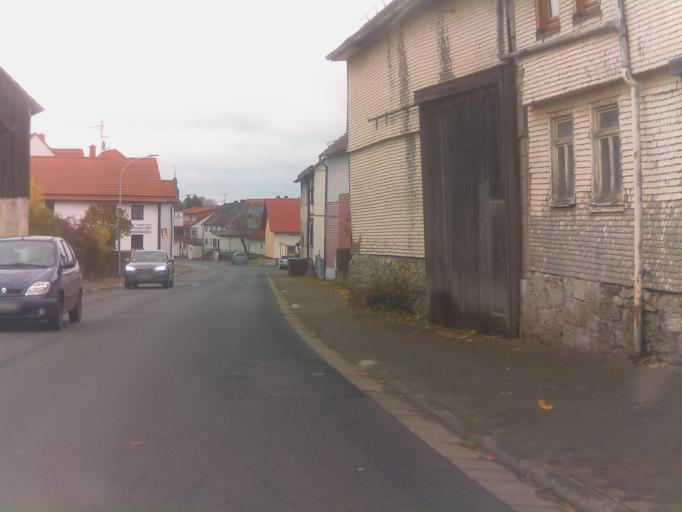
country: DE
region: Hesse
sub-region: Regierungsbezirk Giessen
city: Grebenhain
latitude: 50.5202
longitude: 9.3237
